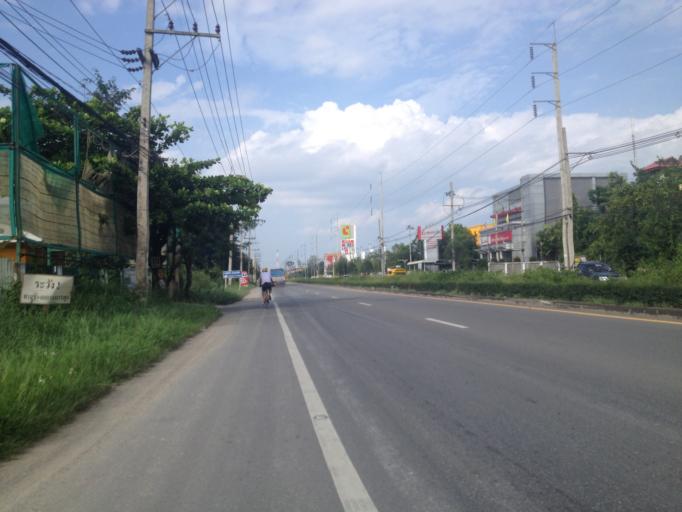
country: TH
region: Chiang Mai
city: Hang Dong
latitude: 18.6668
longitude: 98.9118
